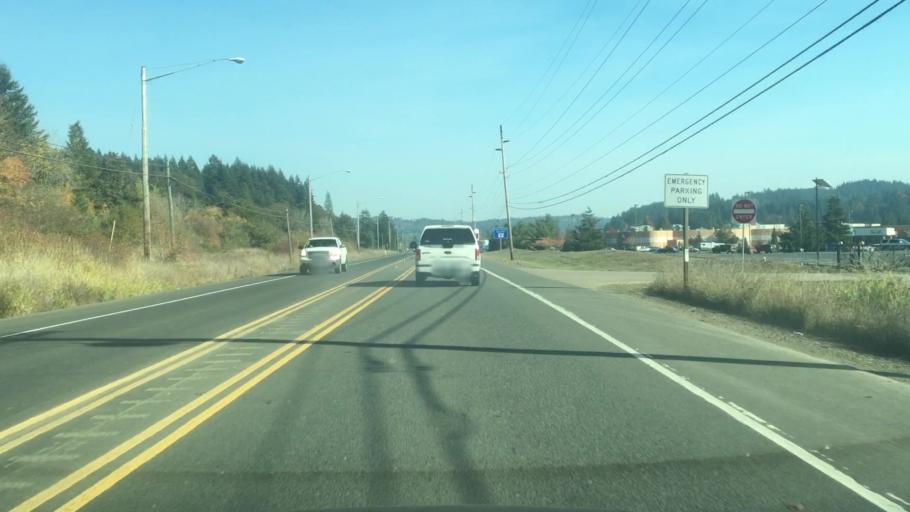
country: US
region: Oregon
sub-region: Polk County
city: Grand Ronde
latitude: 45.0595
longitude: -123.5872
